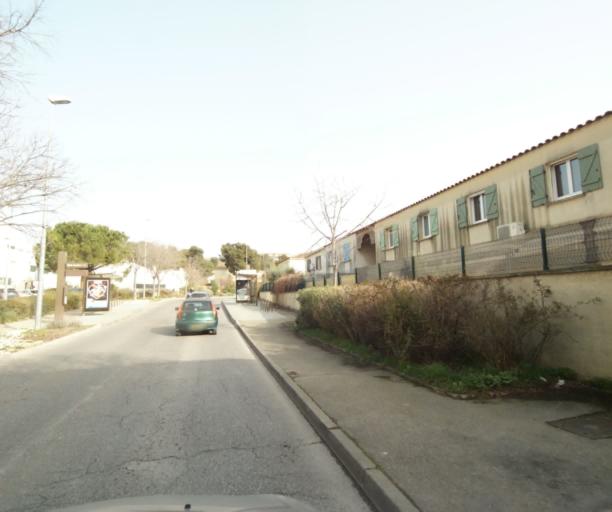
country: FR
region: Provence-Alpes-Cote d'Azur
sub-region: Departement des Bouches-du-Rhone
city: Les Pennes-Mirabeau
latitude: 43.4260
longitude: 5.2797
